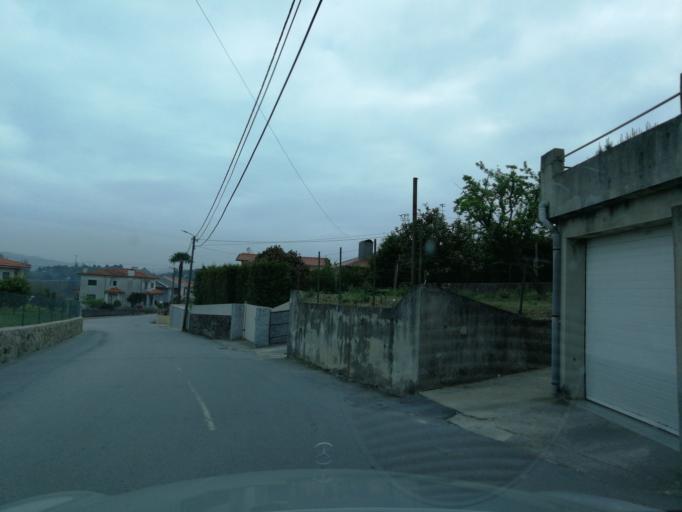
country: PT
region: Braga
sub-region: Braga
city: Braga
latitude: 41.5710
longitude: -8.4345
